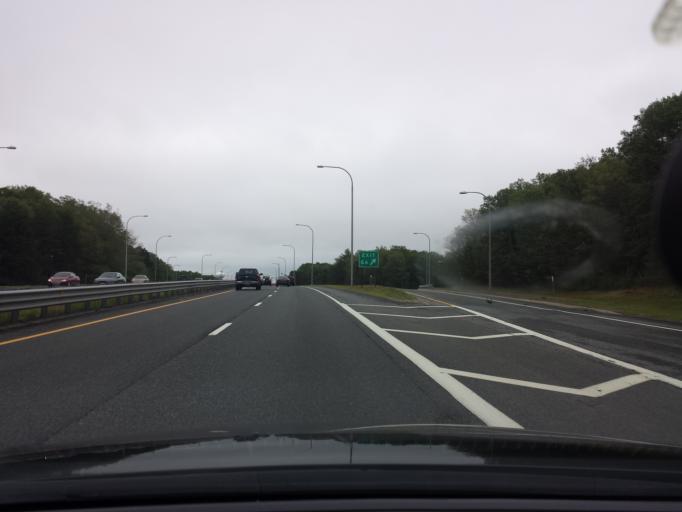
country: US
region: Rhode Island
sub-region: Kent County
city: West Warwick
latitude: 41.6507
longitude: -71.5807
